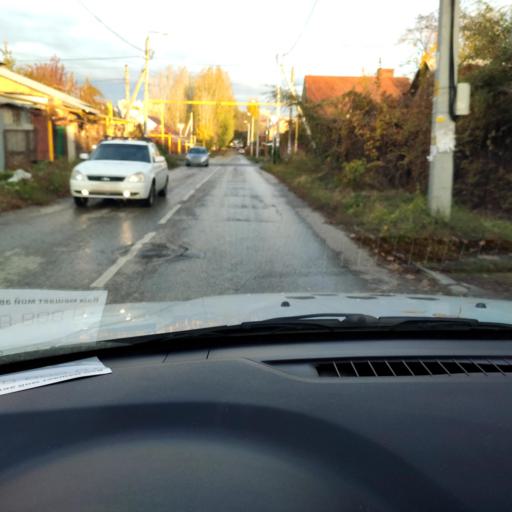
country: RU
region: Samara
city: Tol'yatti
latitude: 53.5252
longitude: 49.4039
